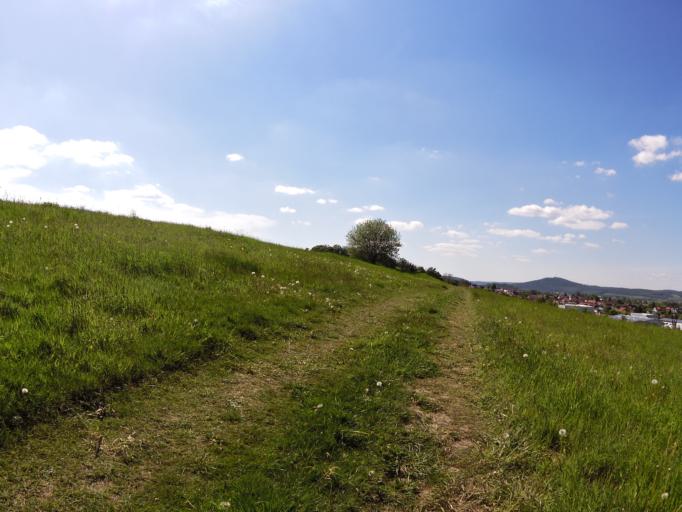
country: DE
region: Thuringia
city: Leimbach
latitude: 50.8097
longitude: 10.2086
